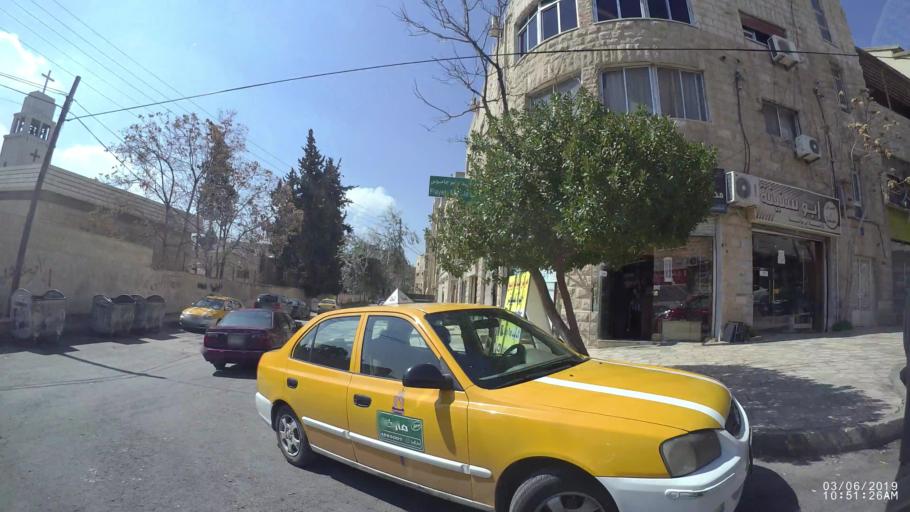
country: JO
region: Amman
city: Amman
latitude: 31.9795
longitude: 35.9862
